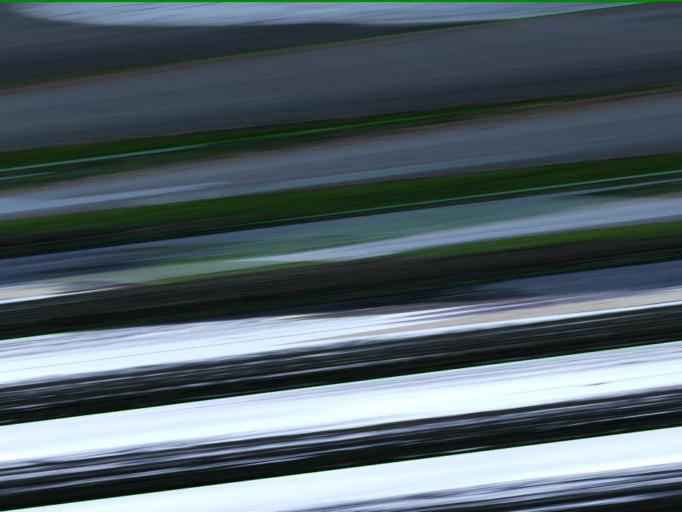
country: FR
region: Ile-de-France
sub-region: Departement des Yvelines
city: Houdan
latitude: 48.7932
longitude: 1.5920
